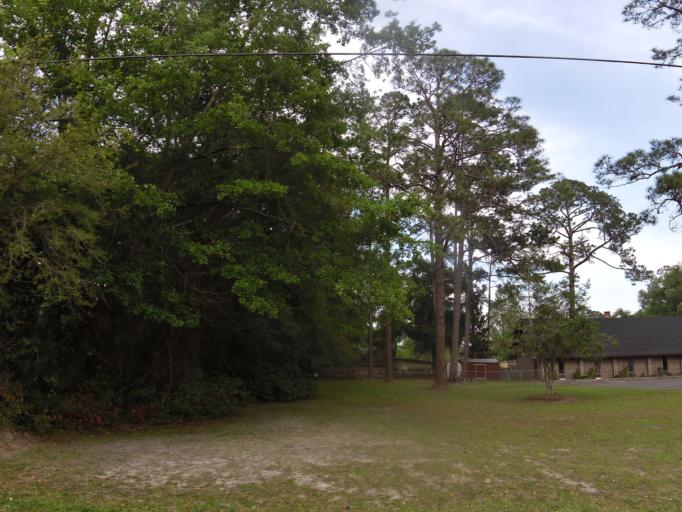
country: US
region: Florida
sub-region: Nassau County
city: Hilliard
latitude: 30.6888
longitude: -81.9229
